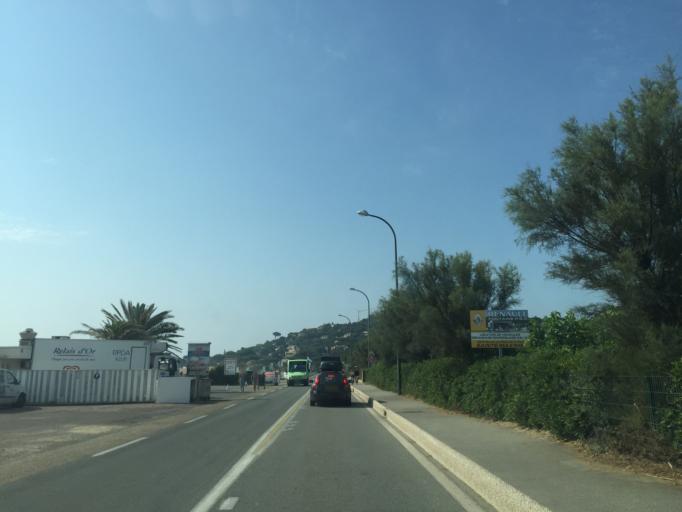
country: FR
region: Provence-Alpes-Cote d'Azur
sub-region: Departement du Var
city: Sainte-Maxime
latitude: 43.3218
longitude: 6.6642
